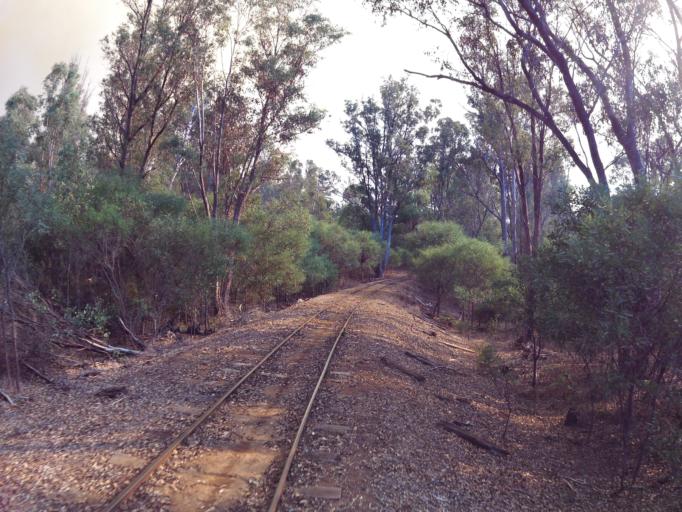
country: AU
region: Western Australia
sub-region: Waroona
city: Waroona
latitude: -32.7386
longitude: 116.1297
